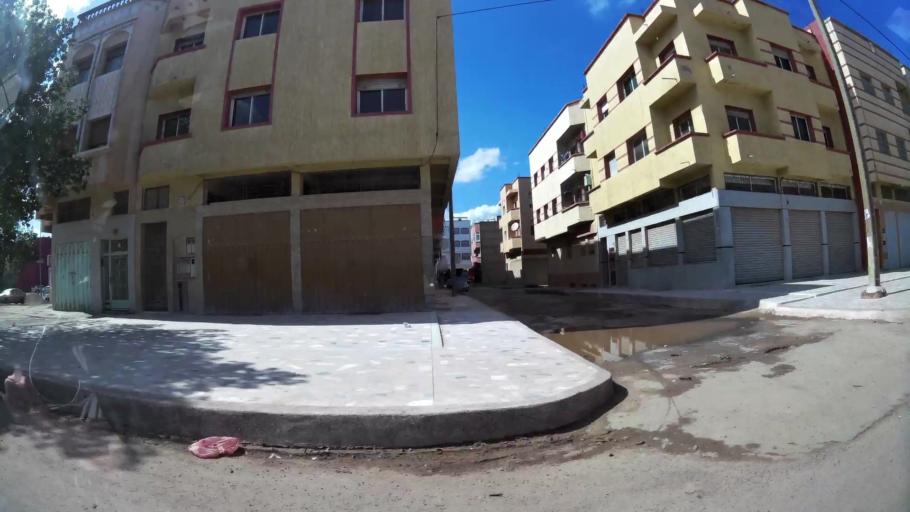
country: MA
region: Grand Casablanca
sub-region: Mediouna
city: Mediouna
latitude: 33.4555
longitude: -7.5134
